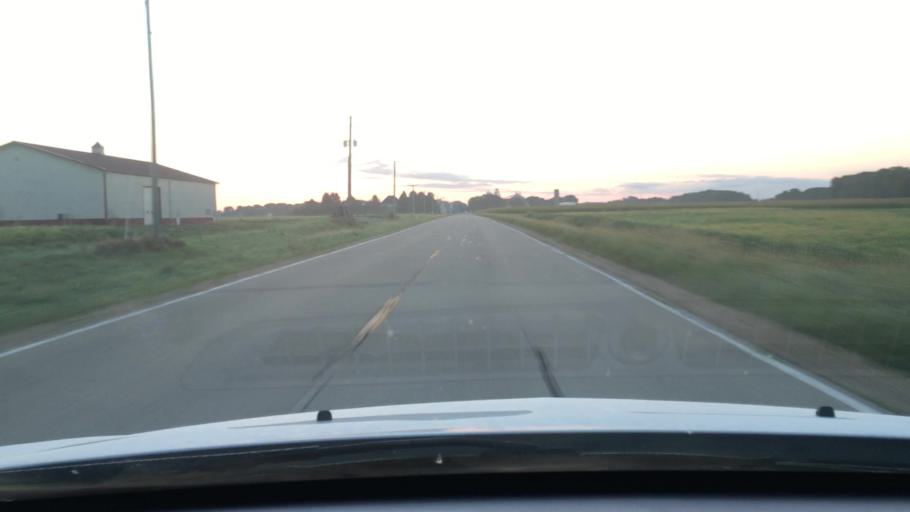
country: US
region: Illinois
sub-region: Ogle County
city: Rochelle
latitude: 41.8472
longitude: -89.0381
